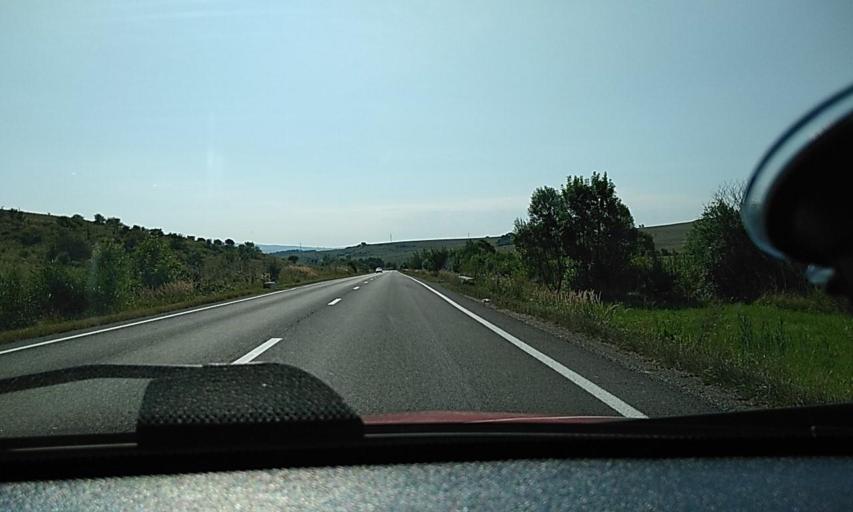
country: RO
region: Brasov
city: Maierus
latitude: 45.9048
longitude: 25.4977
